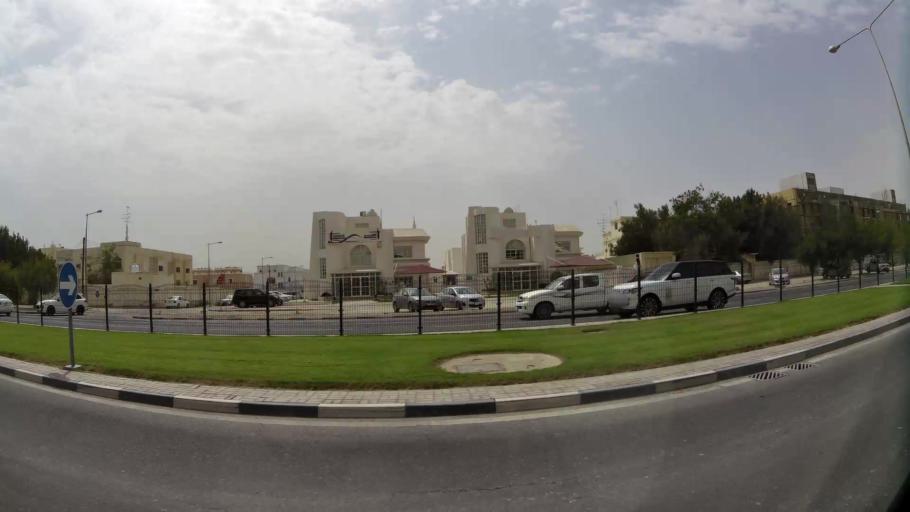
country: QA
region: Baladiyat ad Dawhah
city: Doha
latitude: 25.3077
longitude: 51.4784
